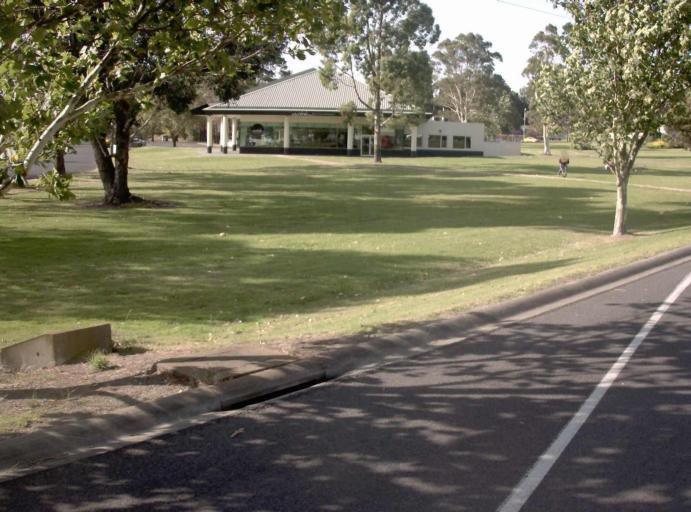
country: AU
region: Victoria
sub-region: Latrobe
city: Morwell
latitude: -38.2383
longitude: 146.4210
